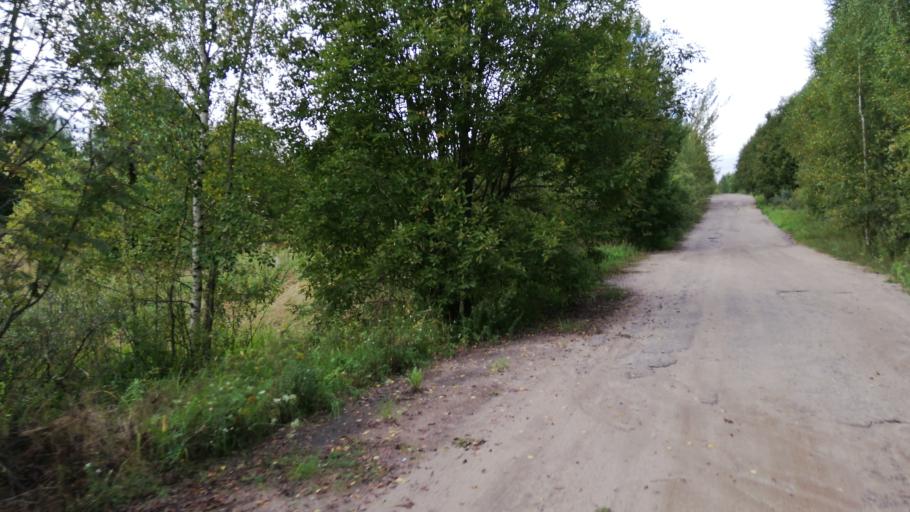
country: RU
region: Jaroslavl
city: Konstantinovskiy
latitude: 57.8006
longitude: 39.7179
